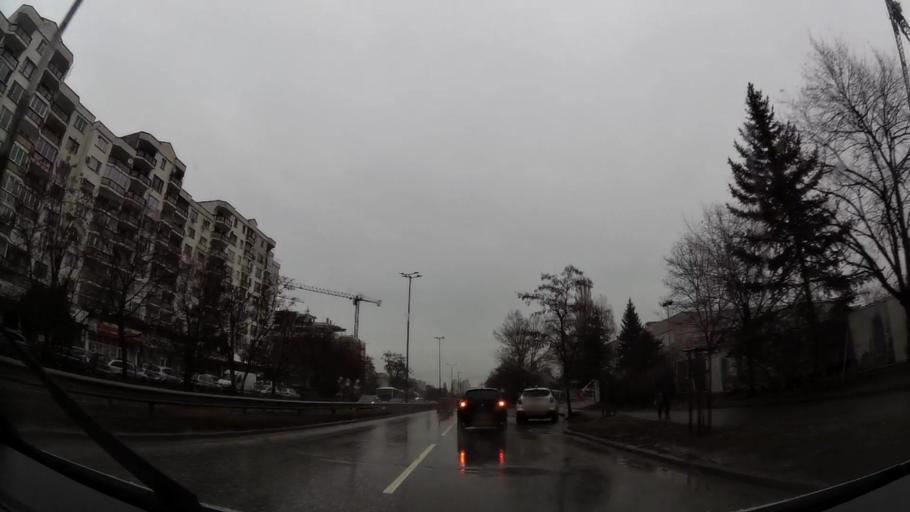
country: BG
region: Sofia-Capital
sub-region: Stolichna Obshtina
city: Sofia
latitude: 42.6619
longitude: 23.3535
